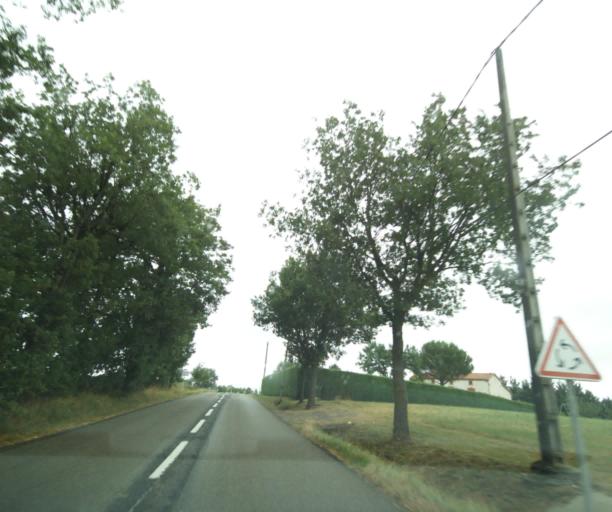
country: FR
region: Midi-Pyrenees
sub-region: Departement du Tarn
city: Le Garric
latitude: 44.0289
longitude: 2.1954
